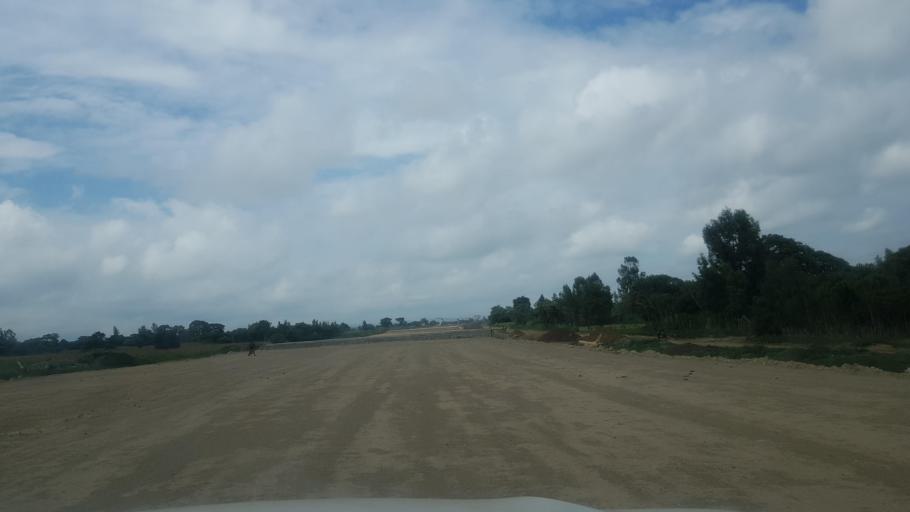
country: ET
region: Oromiya
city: Shashemene
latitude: 7.2637
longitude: 38.5965
